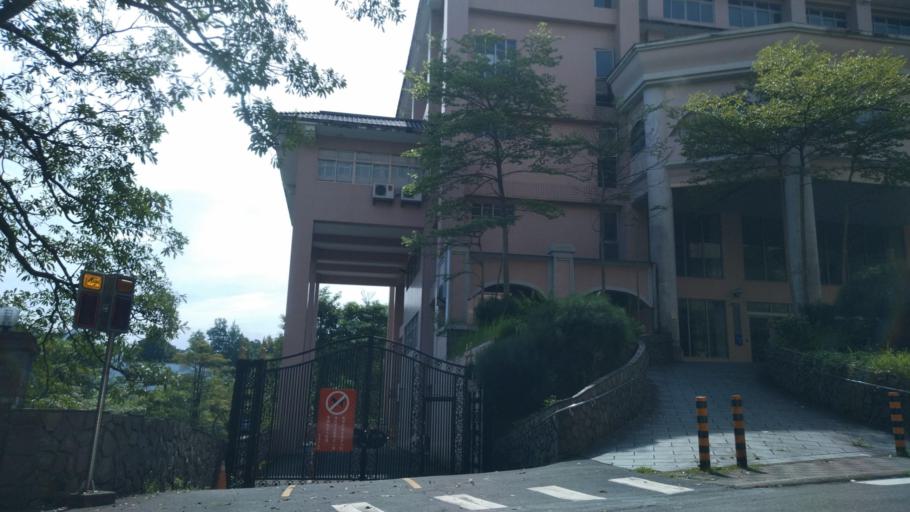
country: TW
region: Taipei
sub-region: Taipei
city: Banqiao
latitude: 24.9508
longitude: 121.5092
